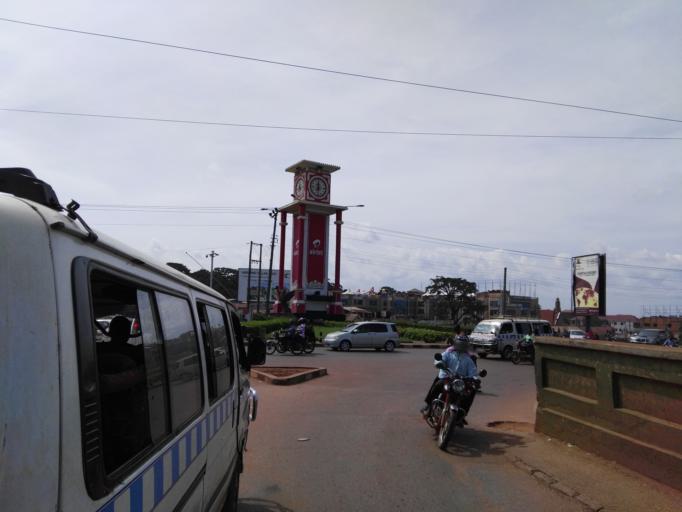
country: UG
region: Central Region
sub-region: Kampala District
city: Kampala
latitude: 0.2931
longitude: 32.5731
